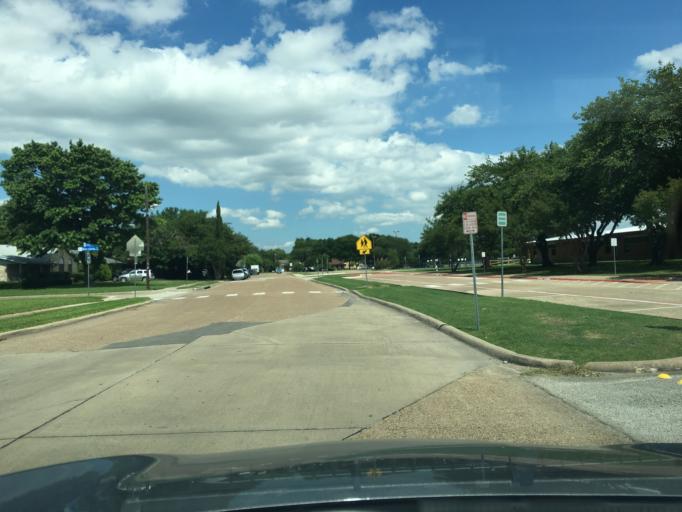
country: US
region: Texas
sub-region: Dallas County
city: Richardson
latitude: 32.9492
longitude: -96.7046
